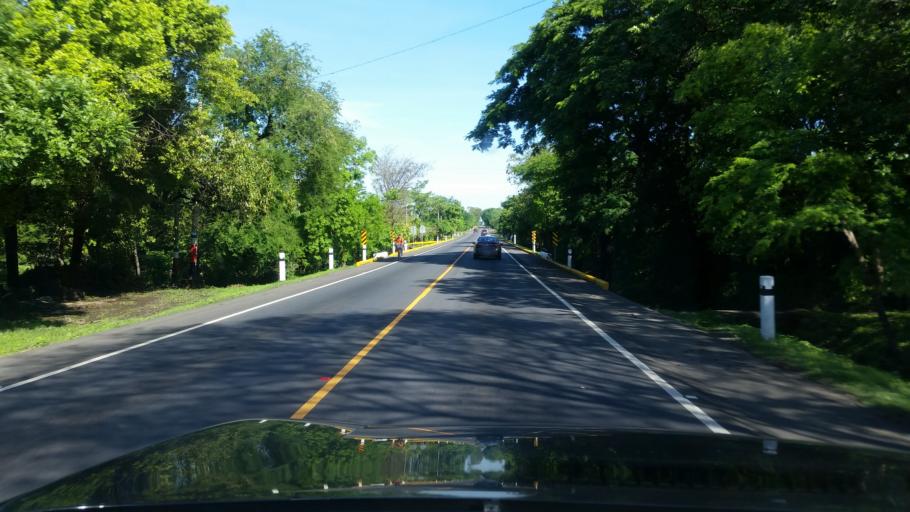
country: NI
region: Chinandega
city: Chichigalpa
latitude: 12.5857
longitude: -87.0108
